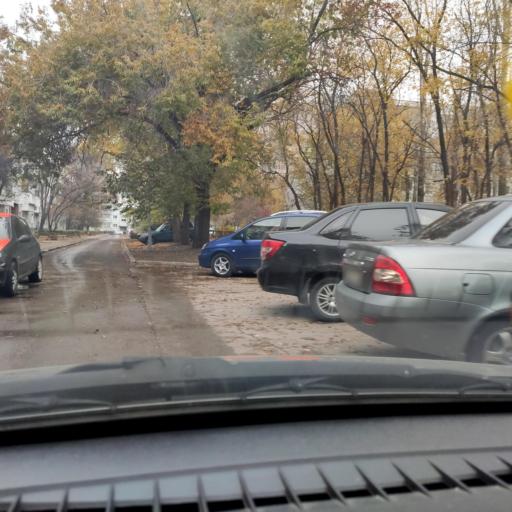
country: RU
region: Samara
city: Tol'yatti
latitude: 53.5245
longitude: 49.3075
